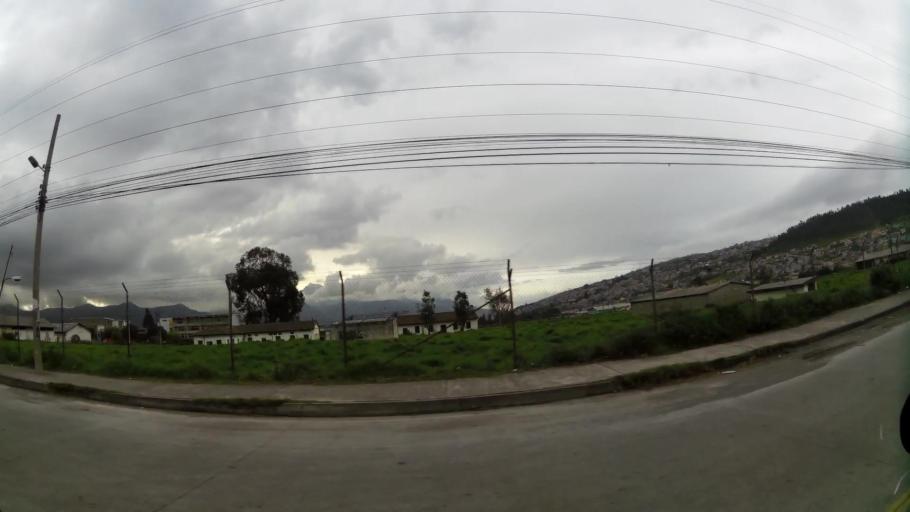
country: EC
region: Pichincha
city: Quito
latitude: -0.3183
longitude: -78.5411
